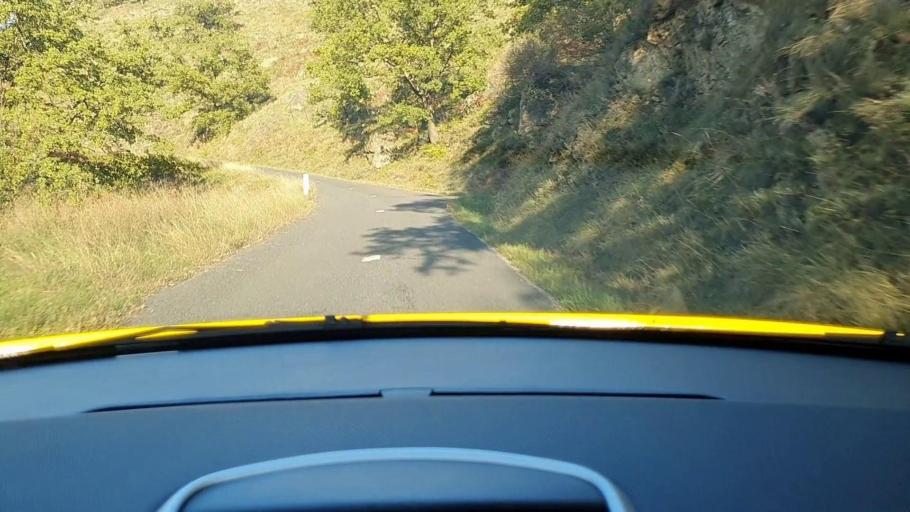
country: FR
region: Languedoc-Roussillon
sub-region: Departement du Gard
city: Sumene
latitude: 43.9829
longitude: 3.7482
